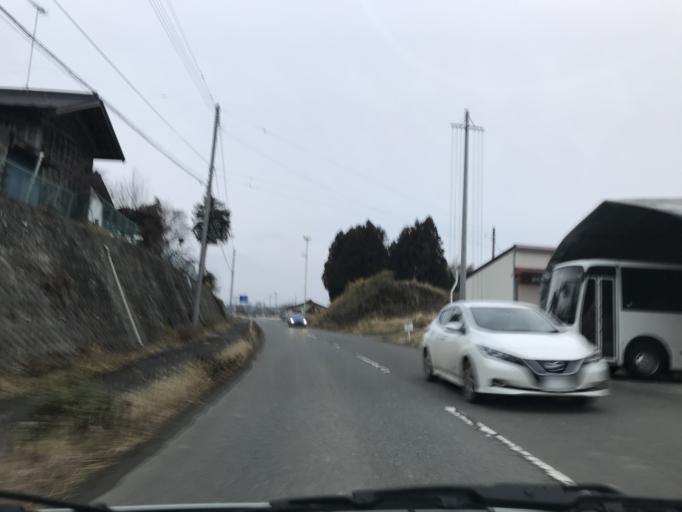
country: JP
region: Miyagi
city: Kogota
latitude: 38.7027
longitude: 141.0985
